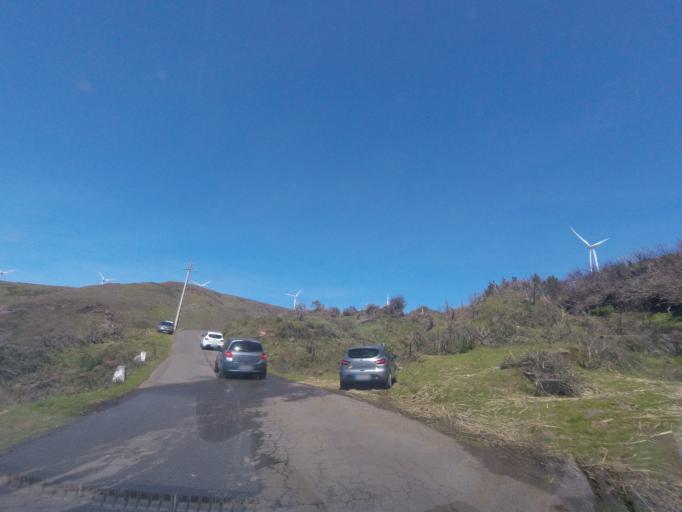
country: PT
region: Madeira
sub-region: Calheta
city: Arco da Calheta
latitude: 32.7389
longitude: -17.1025
